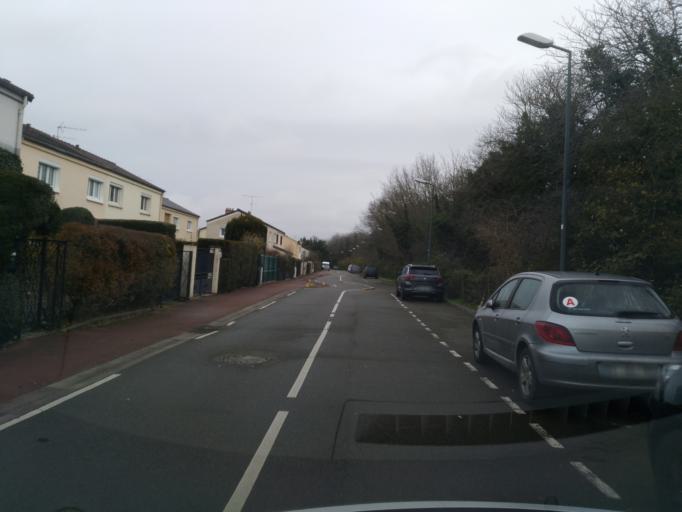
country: FR
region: Ile-de-France
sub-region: Departement des Yvelines
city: Villepreux
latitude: 48.8253
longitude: 2.0034
